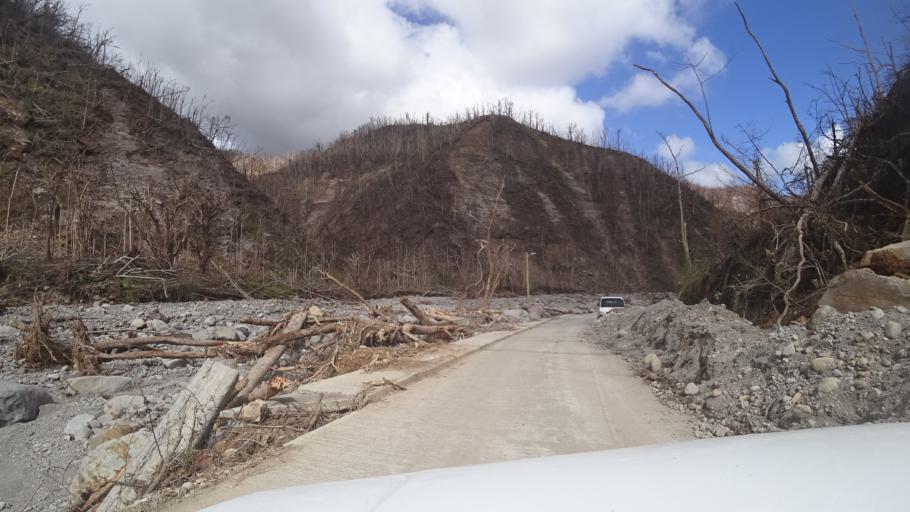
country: DM
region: Saint Patrick
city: Berekua
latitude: 15.2644
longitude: -61.3219
